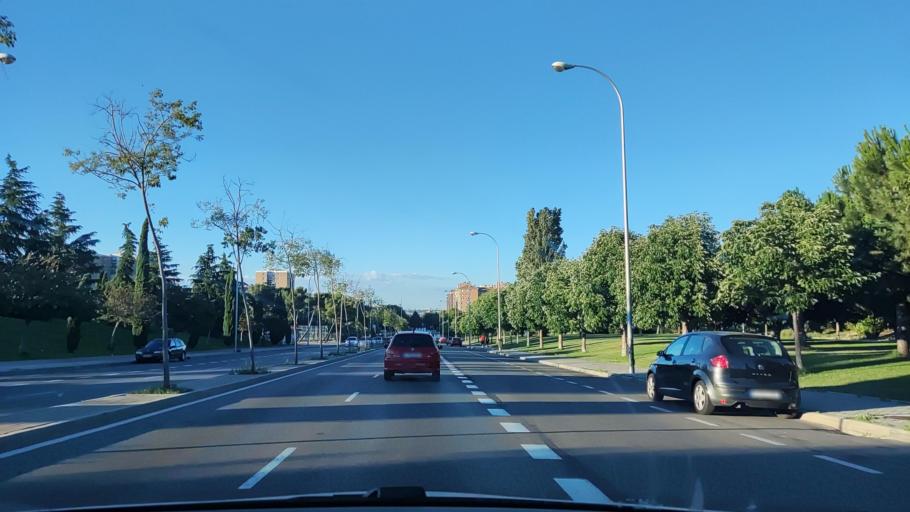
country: ES
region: Madrid
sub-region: Provincia de Madrid
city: Latina
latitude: 40.3711
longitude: -3.7370
